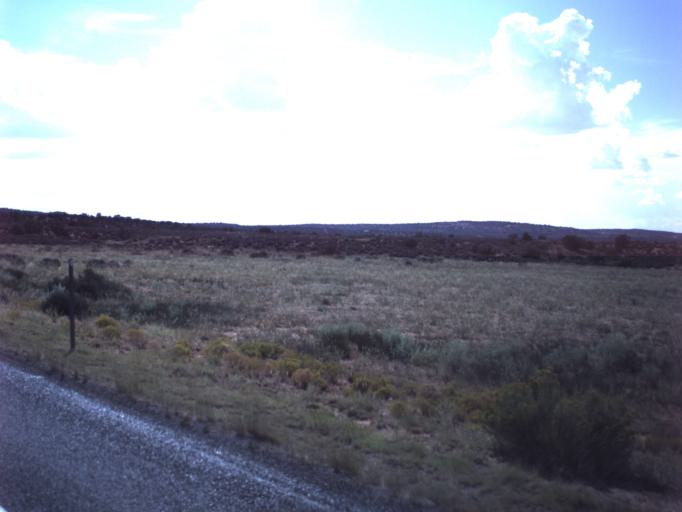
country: US
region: Utah
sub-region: Grand County
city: Moab
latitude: 38.6136
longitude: -109.8158
